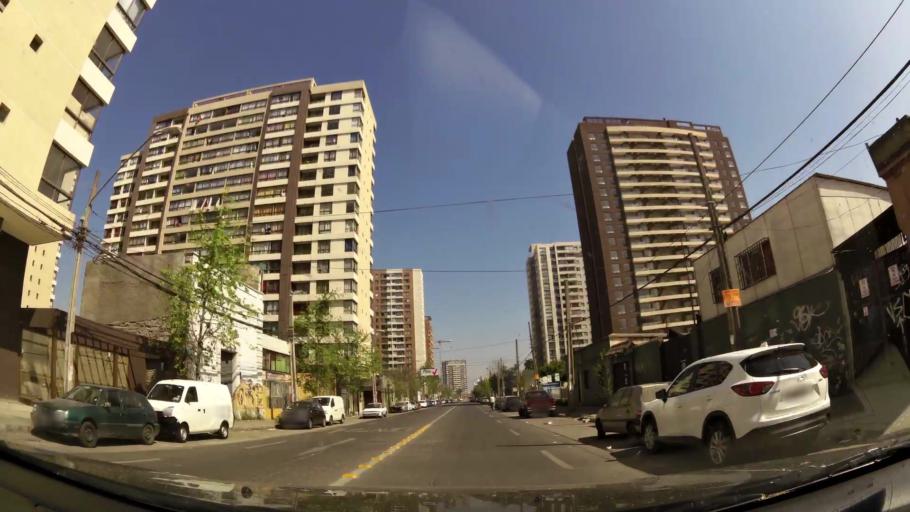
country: CL
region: Santiago Metropolitan
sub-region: Provincia de Santiago
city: Santiago
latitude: -33.4070
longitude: -70.6625
